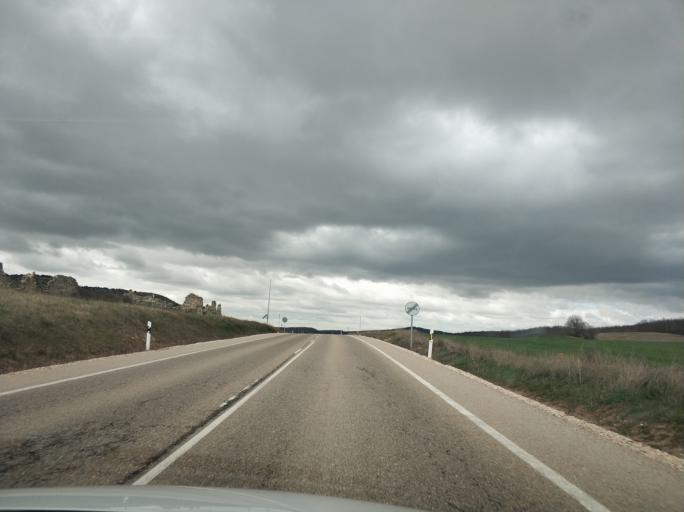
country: ES
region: Castille and Leon
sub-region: Provincia de Burgos
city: Cuevas de San Clemente
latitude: 42.1146
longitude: -3.5278
